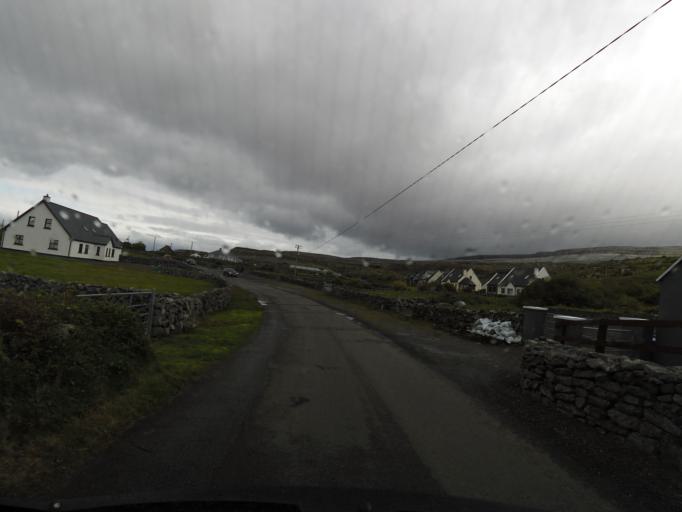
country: IE
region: Connaught
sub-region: County Galway
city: Bearna
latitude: 53.1317
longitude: -9.2752
